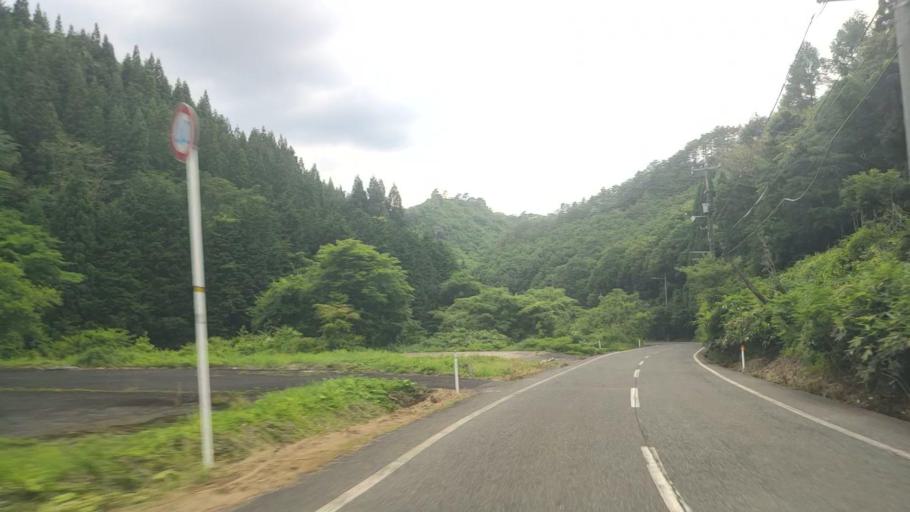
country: JP
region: Tottori
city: Kurayoshi
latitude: 35.2942
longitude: 133.9851
